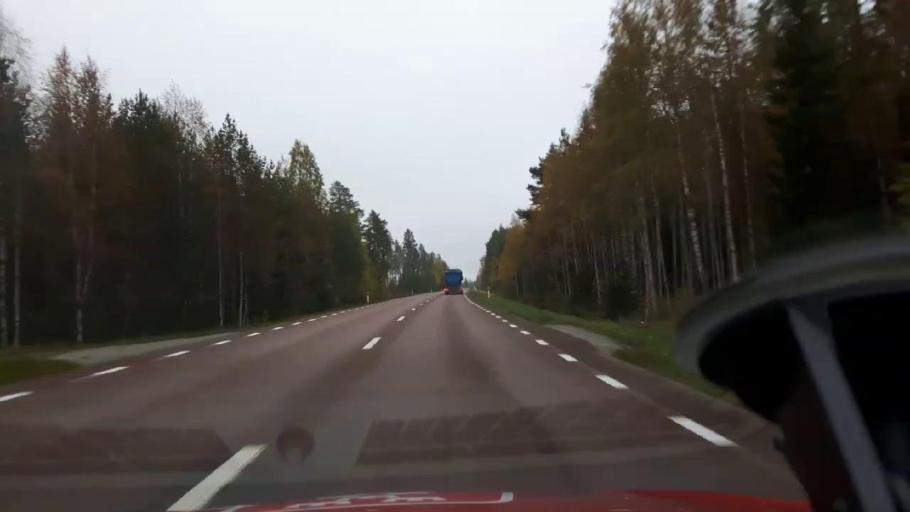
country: SE
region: Jaemtland
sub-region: Bergs Kommun
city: Hoverberg
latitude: 62.5997
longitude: 14.4177
